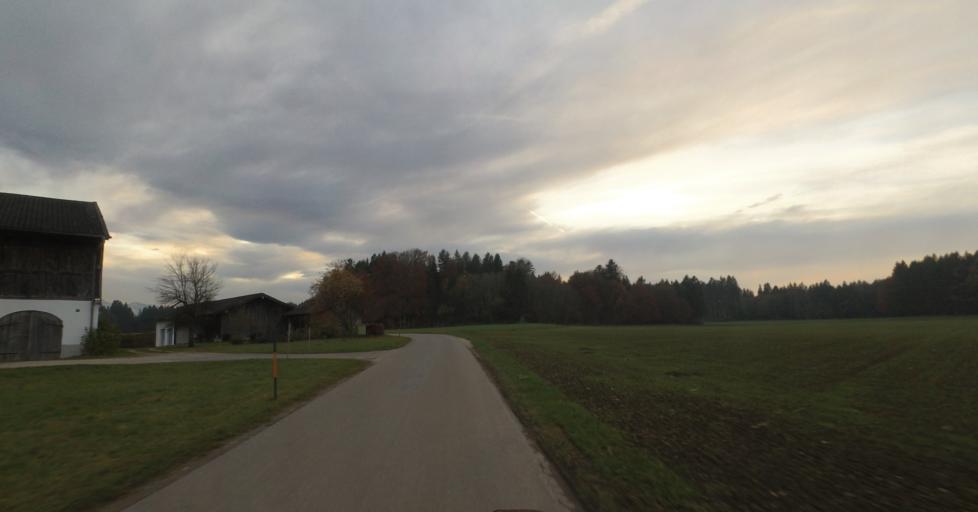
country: DE
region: Bavaria
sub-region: Upper Bavaria
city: Gstadt am Chiemsee
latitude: 47.9075
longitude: 12.4217
